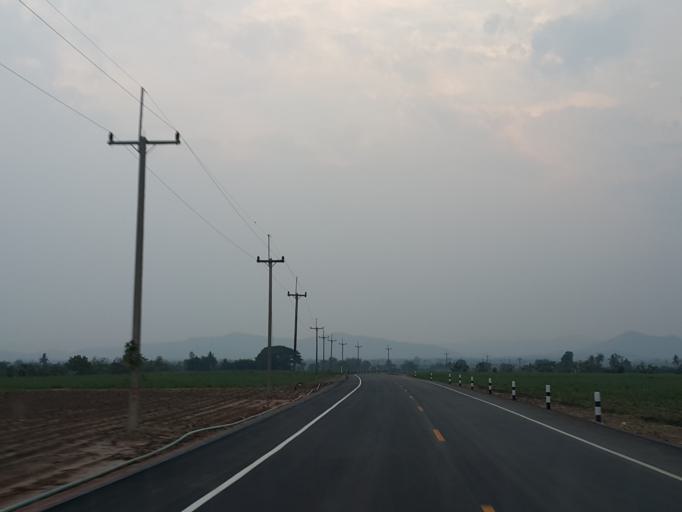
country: TH
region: Suphan Buri
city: Dan Chang
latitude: 14.9407
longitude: 99.6469
